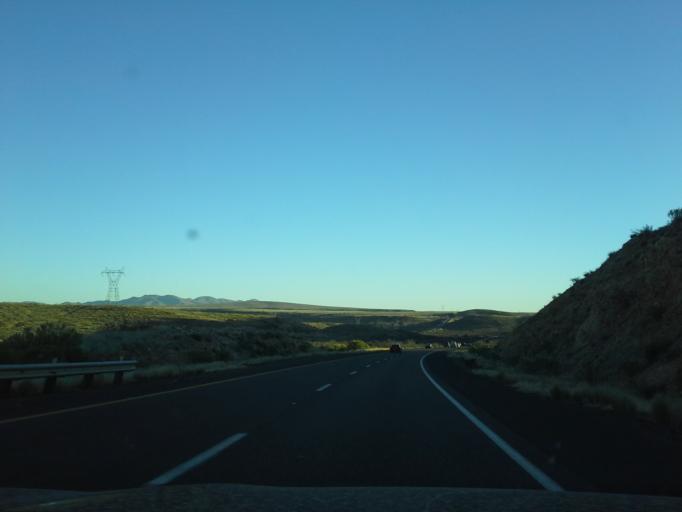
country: US
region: Arizona
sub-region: Yavapai County
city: Cordes Lakes
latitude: 34.2534
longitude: -112.1142
